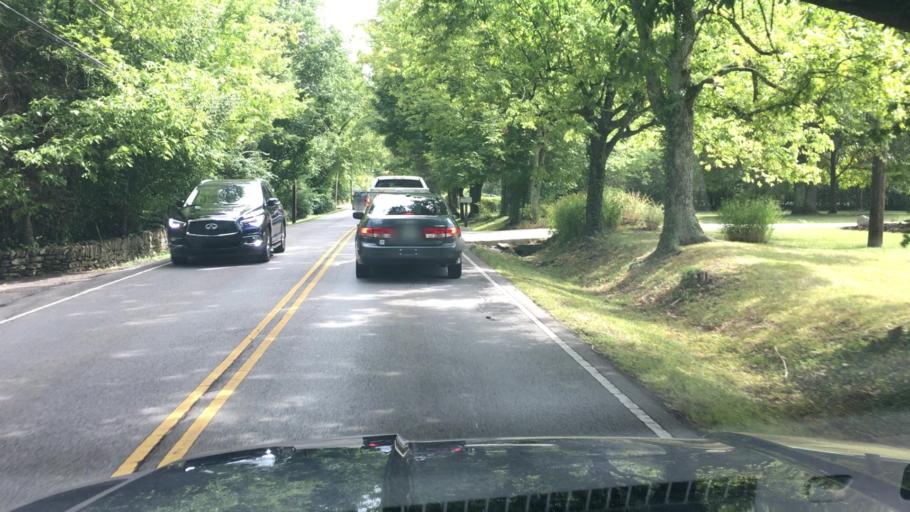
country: US
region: Tennessee
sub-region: Davidson County
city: Oak Hill
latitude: 36.0818
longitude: -86.8053
